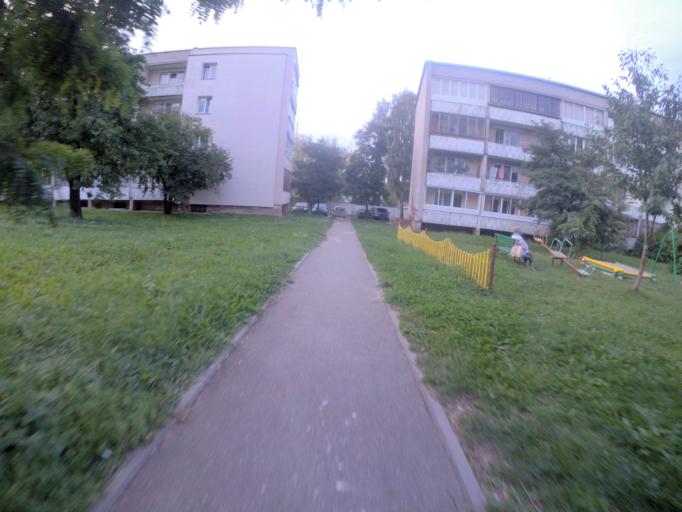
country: BY
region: Grodnenskaya
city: Hrodna
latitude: 53.6925
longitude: 23.8257
